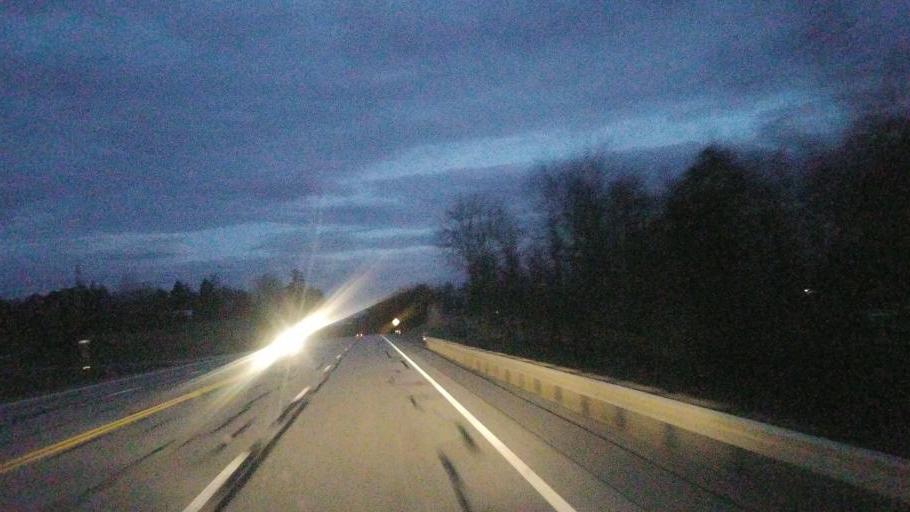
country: US
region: Tennessee
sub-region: Sequatchie County
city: Dunlap
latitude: 35.4818
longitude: -85.4646
